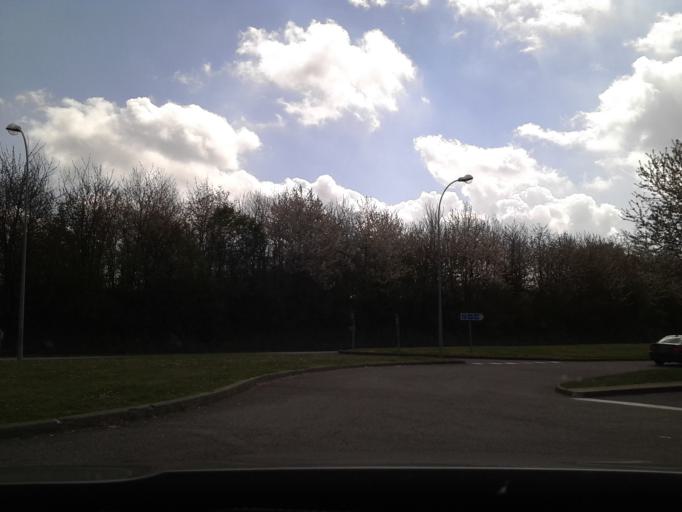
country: FR
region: Brittany
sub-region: Departement d'Ille-et-Vilaine
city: La Dominelais
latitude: 47.8007
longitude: -1.6904
